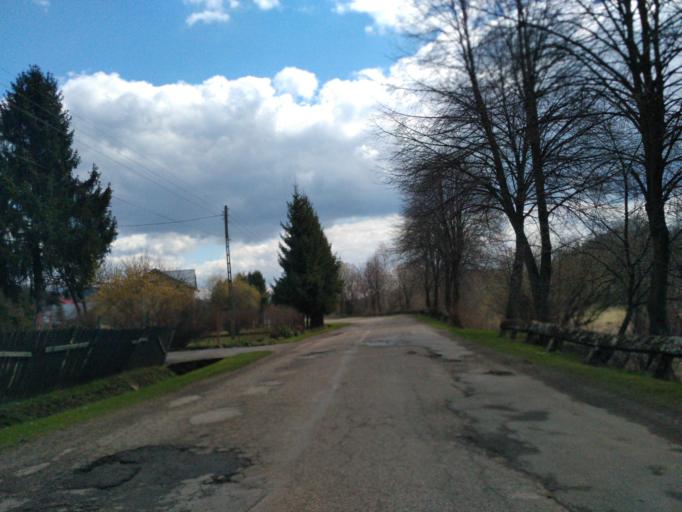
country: PL
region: Subcarpathian Voivodeship
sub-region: Powiat sanocki
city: Tyrawa Woloska
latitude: 49.6069
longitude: 22.2950
